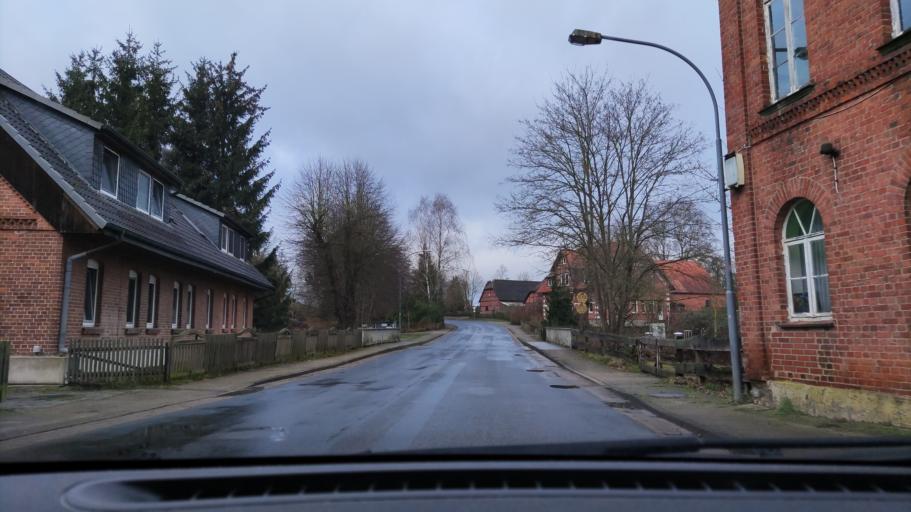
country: DE
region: Lower Saxony
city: Natendorf
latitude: 53.0805
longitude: 10.4678
